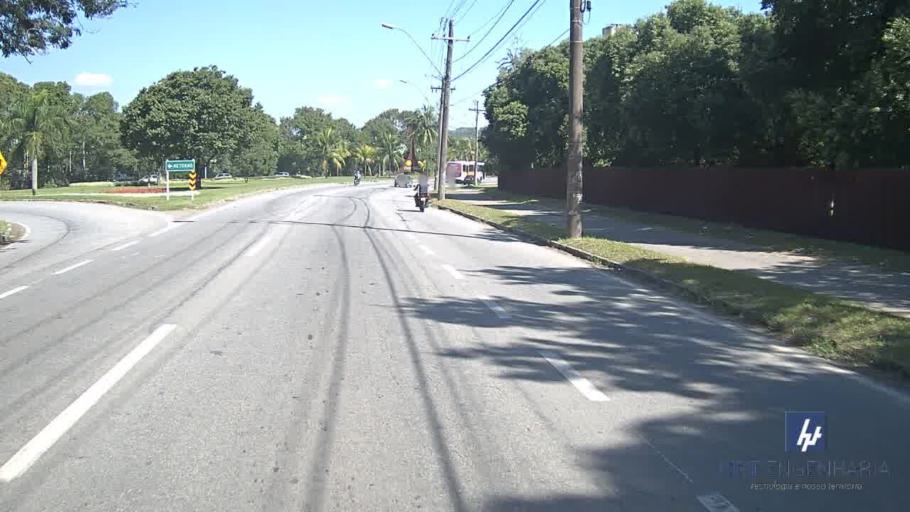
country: BR
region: Minas Gerais
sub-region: Ipatinga
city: Ipatinga
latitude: -19.4850
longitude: -42.5554
